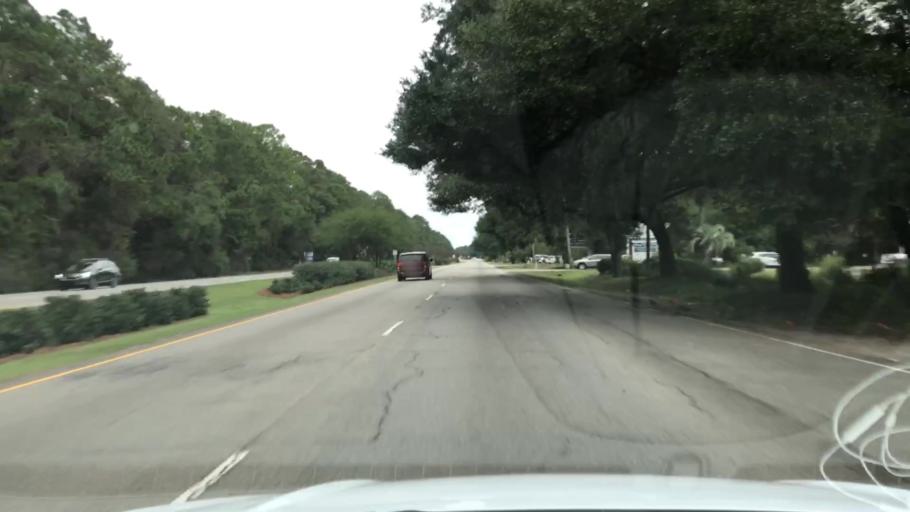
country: US
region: South Carolina
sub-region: Georgetown County
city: Murrells Inlet
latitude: 33.4919
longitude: -79.0896
